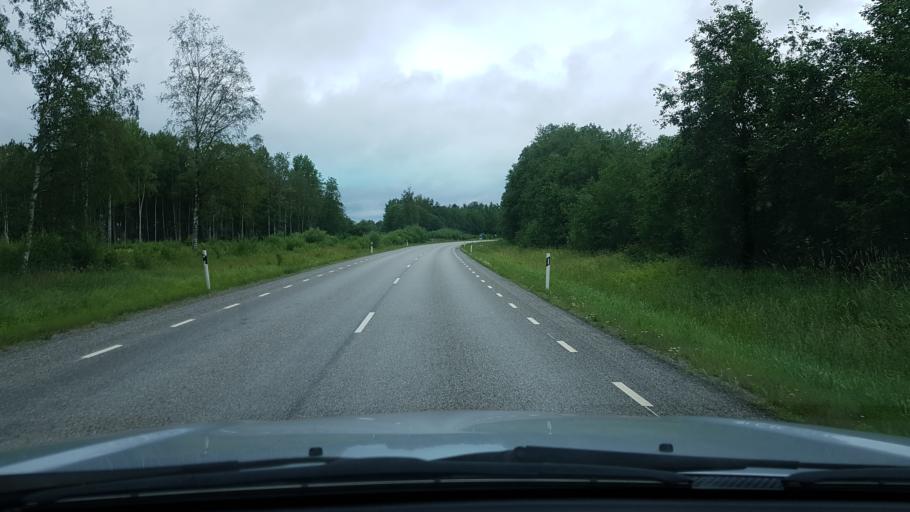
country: EE
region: Ida-Virumaa
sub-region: Narva-Joesuu linn
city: Narva-Joesuu
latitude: 59.3479
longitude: 27.9323
